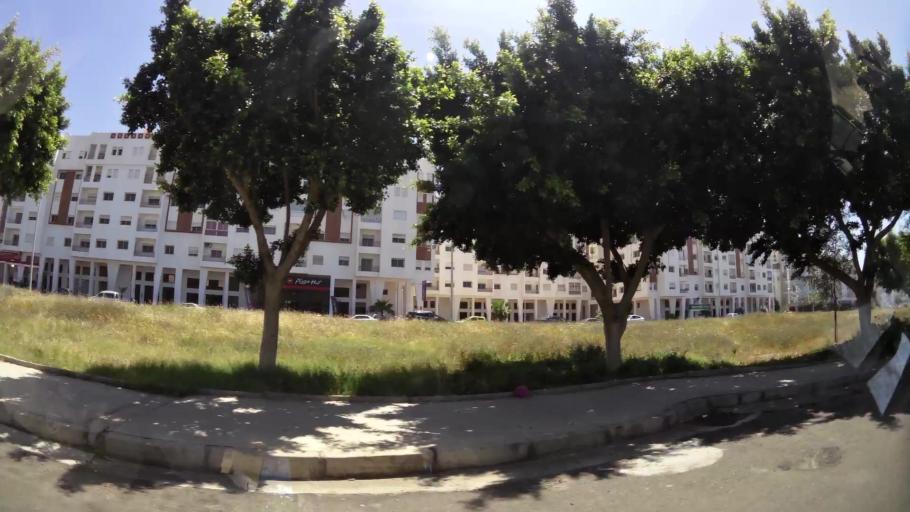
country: MA
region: Souss-Massa-Draa
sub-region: Agadir-Ida-ou-Tnan
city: Agadir
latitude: 30.4333
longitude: -9.5827
